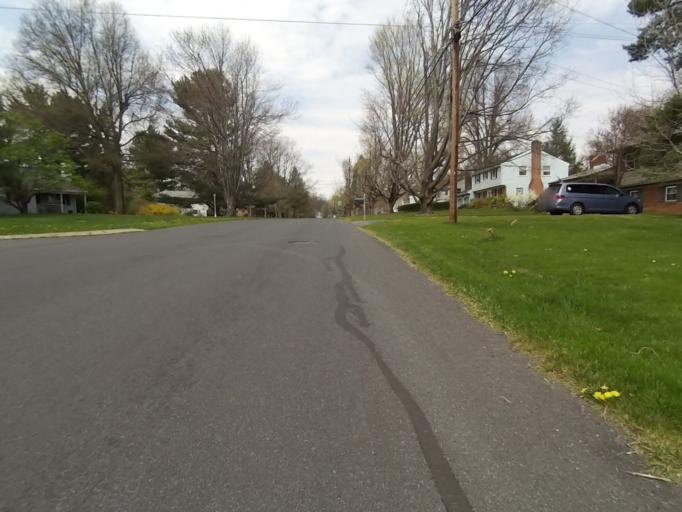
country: US
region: Pennsylvania
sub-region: Centre County
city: Park Forest Village
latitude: 40.7969
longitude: -77.8961
